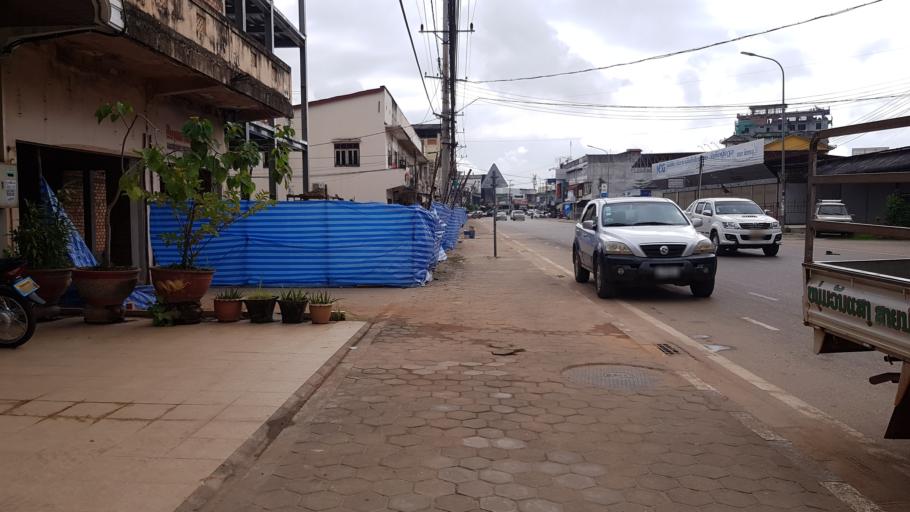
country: LA
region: Vientiane
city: Vientiane
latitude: 17.9695
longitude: 102.6000
